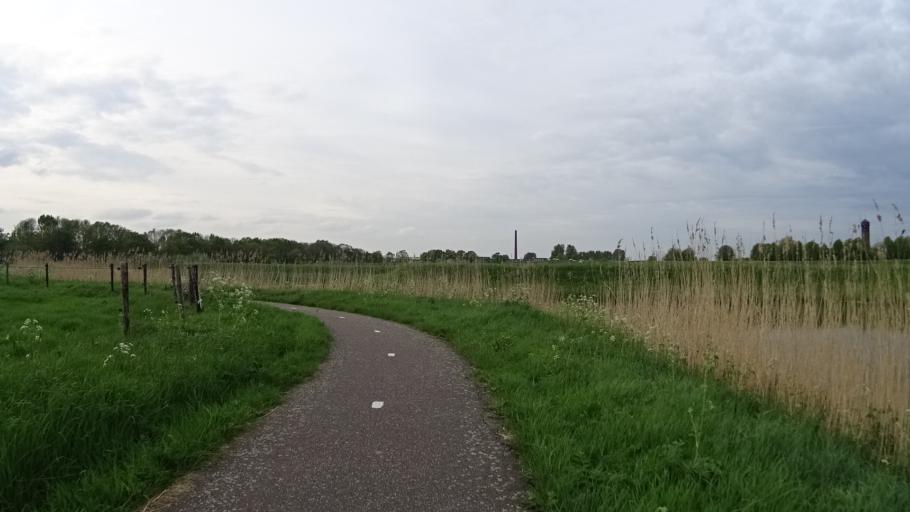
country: NL
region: North Brabant
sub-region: Gemeente Heusden
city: Heusden
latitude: 51.7307
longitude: 5.1305
